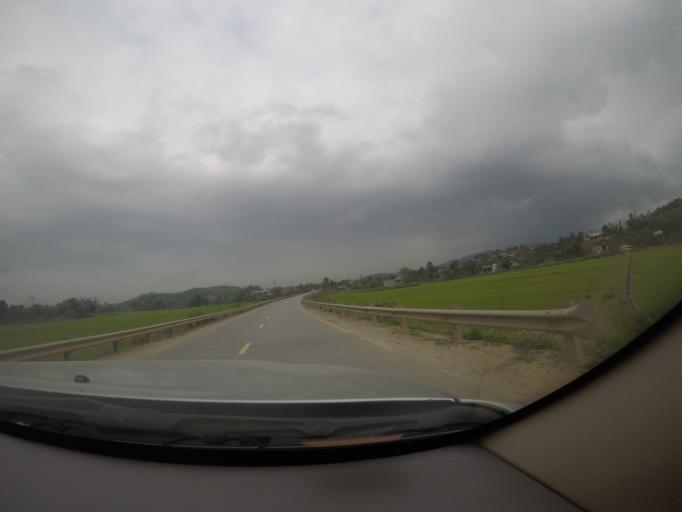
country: VN
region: Quang Binh
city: Ba Don
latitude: 17.6162
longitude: 106.3630
